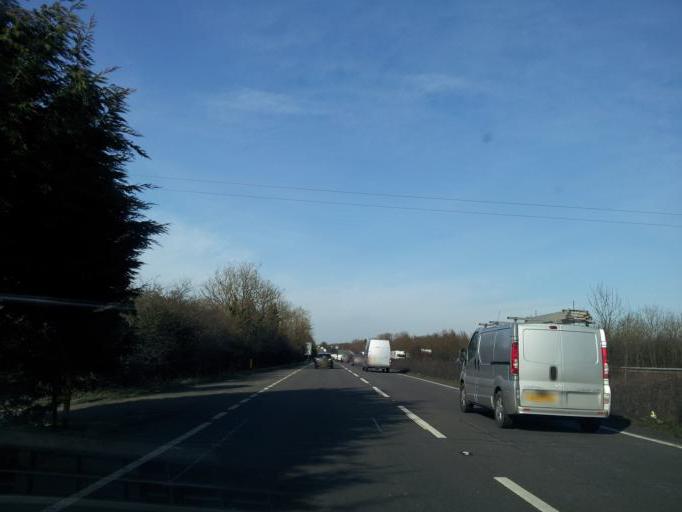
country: GB
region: England
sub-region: District of Rutland
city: Clipsham
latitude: 52.7232
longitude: -0.5963
